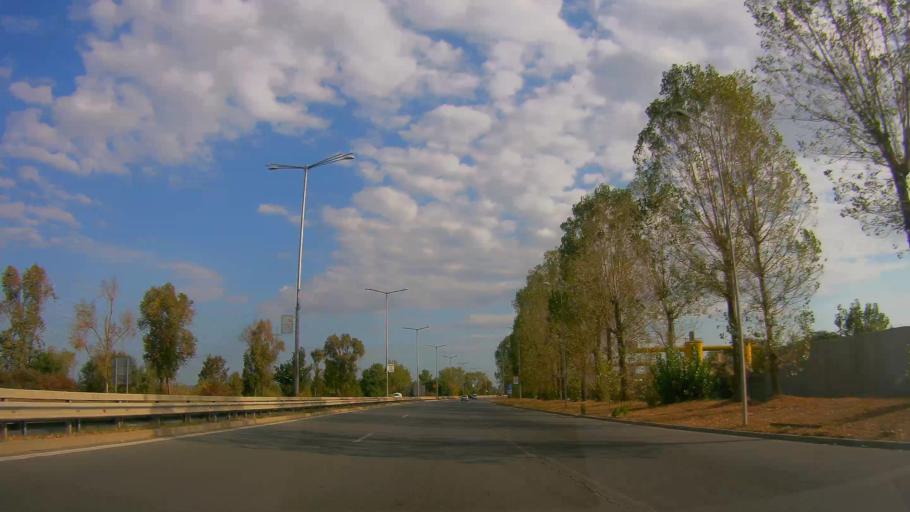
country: BG
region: Burgas
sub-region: Obshtina Burgas
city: Burgas
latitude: 42.4780
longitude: 27.4360
